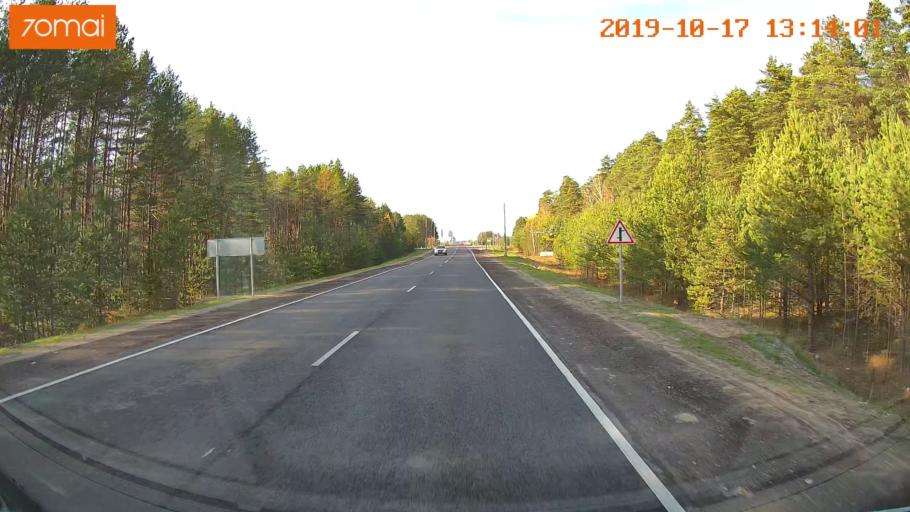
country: RU
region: Rjazan
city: Gus'-Zheleznyy
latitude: 55.0496
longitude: 41.1792
